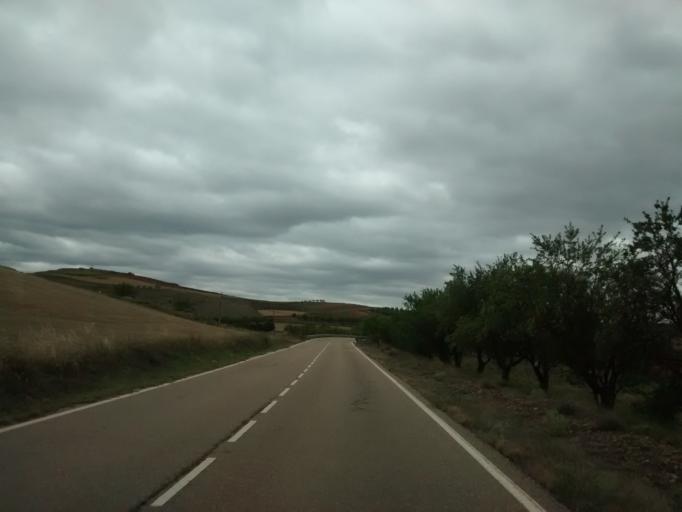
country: ES
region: Aragon
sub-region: Provincia de Zaragoza
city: Trasmoz
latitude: 41.8389
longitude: -1.7125
